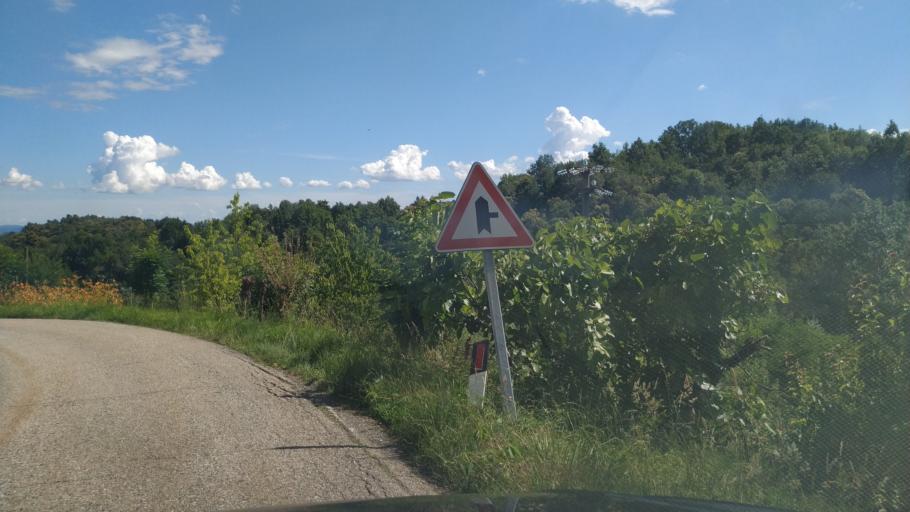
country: IT
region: Piedmont
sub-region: Provincia di Torino
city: Baldissero Canavese
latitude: 45.4115
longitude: 7.7168
